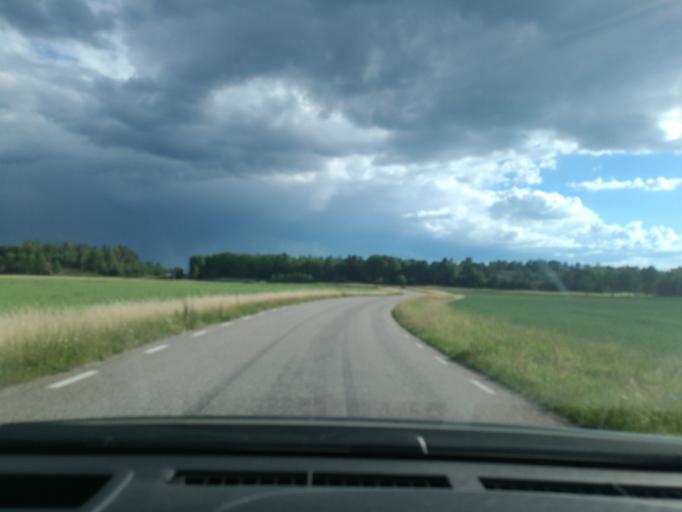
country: SE
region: Soedermanland
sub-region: Eskilstuna Kommun
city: Arla
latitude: 59.4175
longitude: 16.7056
